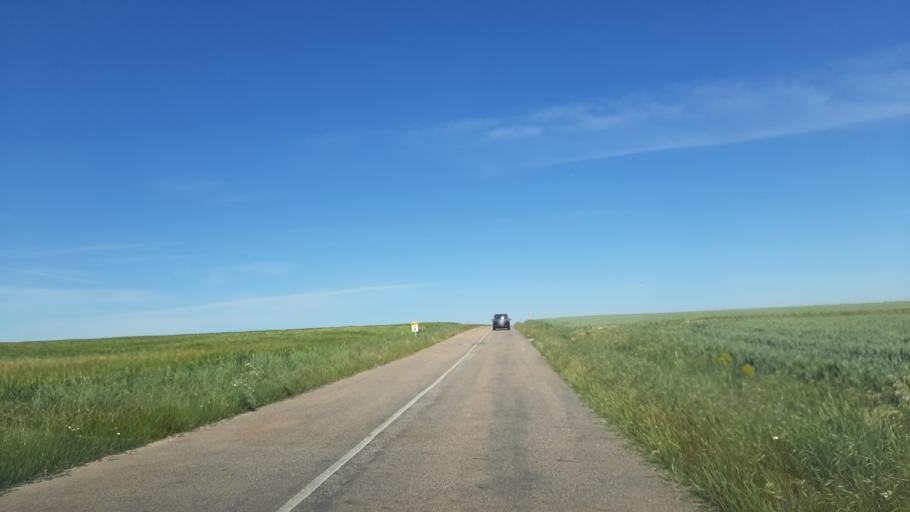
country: ES
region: Castille and Leon
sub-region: Provincia de Salamanca
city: Pedrosillo de Alba
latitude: 40.8220
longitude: -5.4151
